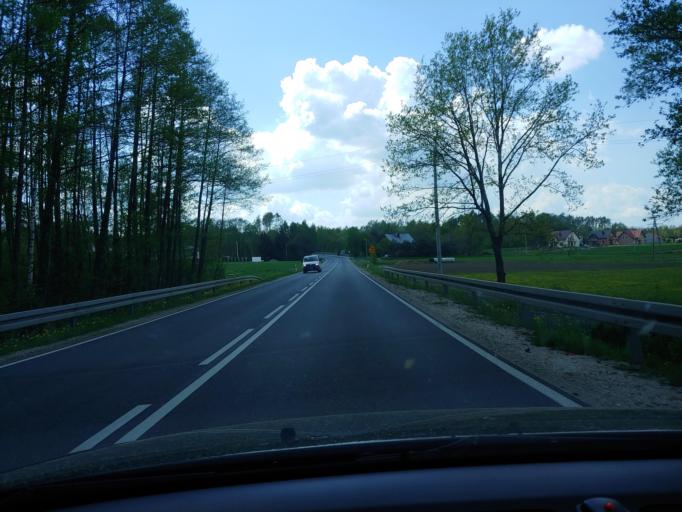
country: PL
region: Lesser Poland Voivodeship
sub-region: Powiat tarnowski
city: Jodlowka-Walki
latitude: 50.1284
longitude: 21.1490
